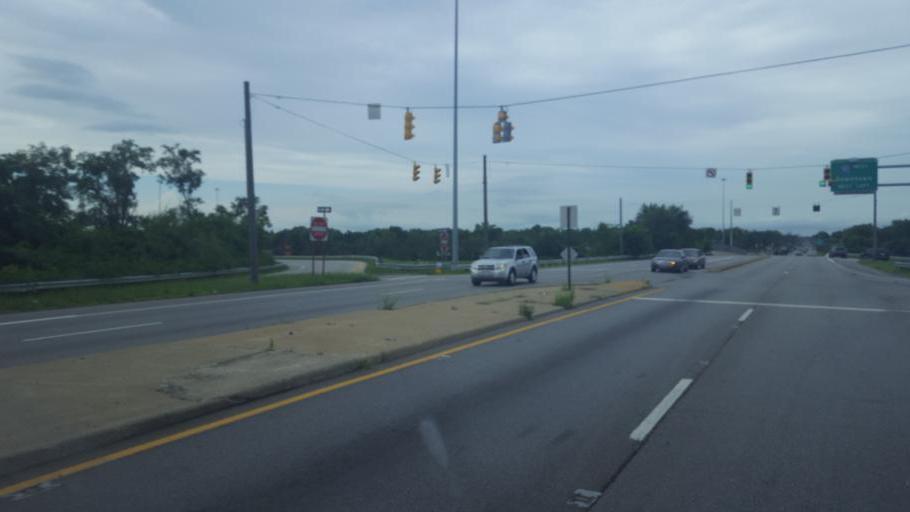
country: US
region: Ohio
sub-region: Franklin County
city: Whitehall
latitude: 39.9349
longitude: -82.8788
